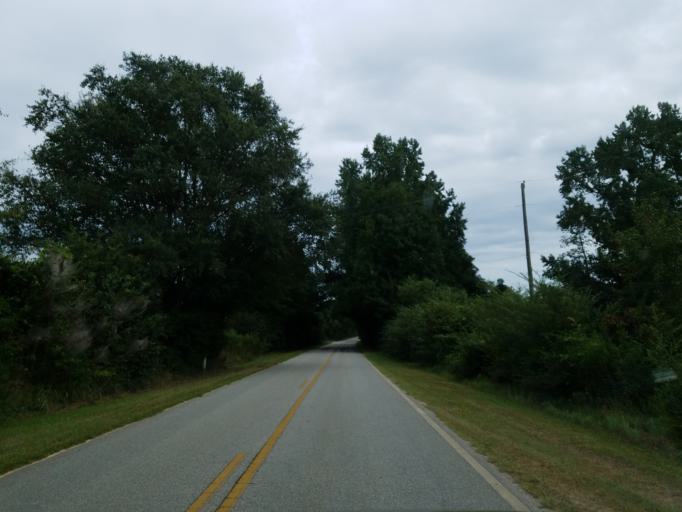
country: US
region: Georgia
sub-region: Lamar County
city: Barnesville
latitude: 33.0034
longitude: -84.0636
